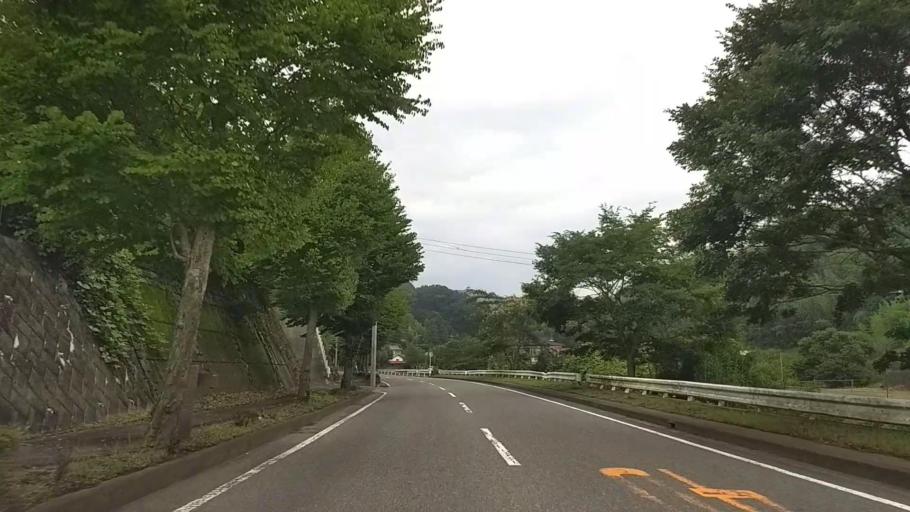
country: JP
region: Kanagawa
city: Hadano
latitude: 35.3344
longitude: 139.2002
